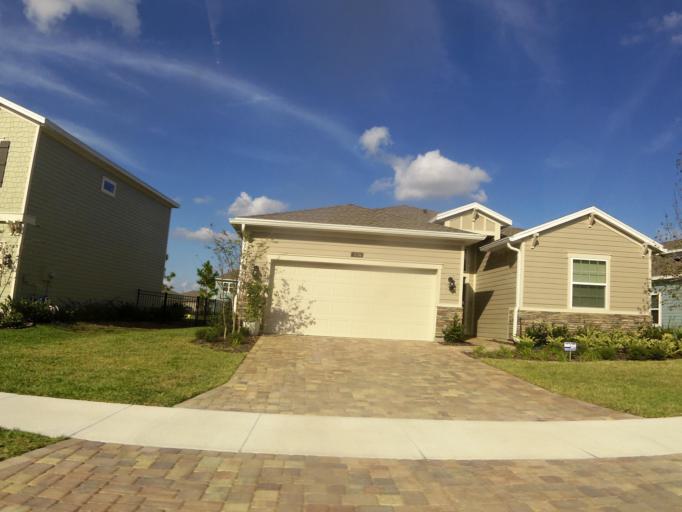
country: US
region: Florida
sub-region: Clay County
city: Green Cove Springs
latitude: 29.9268
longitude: -81.5168
